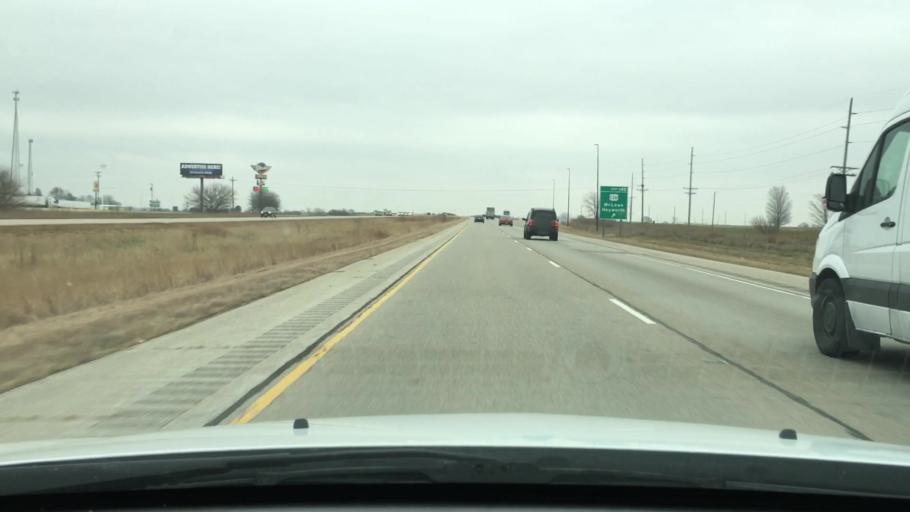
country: US
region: Illinois
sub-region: Logan County
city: Atlanta
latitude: 40.3075
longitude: -89.1708
